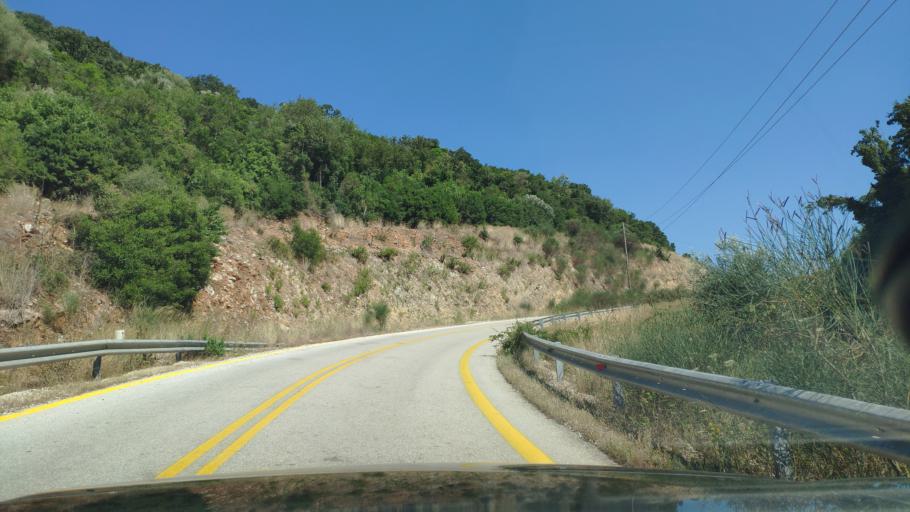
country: GR
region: West Greece
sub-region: Nomos Aitolias kai Akarnanias
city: Amfilochia
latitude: 38.8594
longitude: 21.0845
